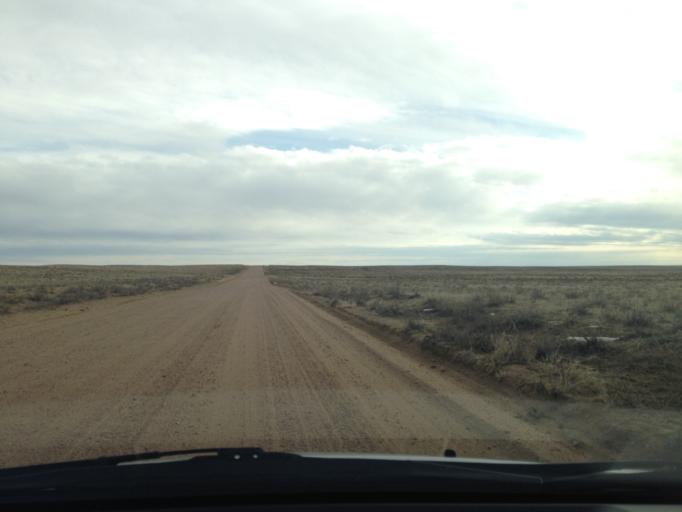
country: US
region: Colorado
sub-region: Weld County
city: Keenesburg
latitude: 40.2417
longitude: -104.2068
